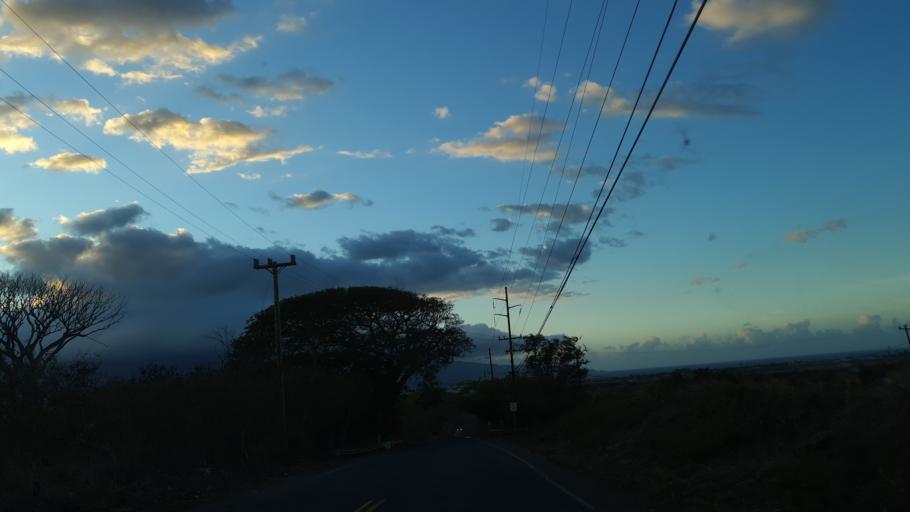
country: US
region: Hawaii
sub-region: Maui County
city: Kahului
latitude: 20.8647
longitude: -156.4311
